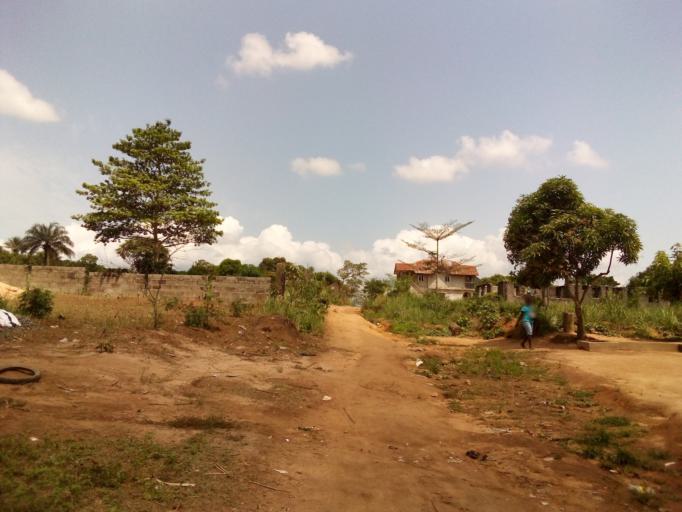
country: SL
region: Western Area
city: Waterloo
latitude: 8.3372
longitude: -13.0217
